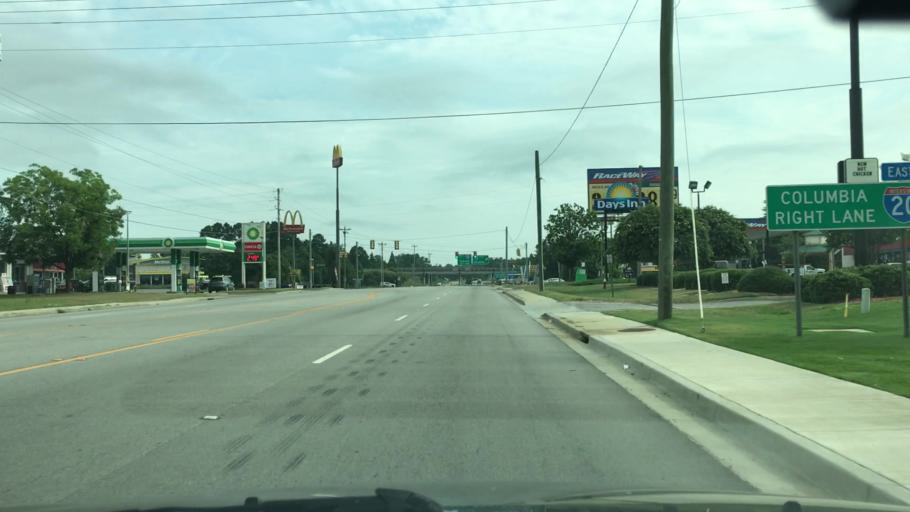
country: US
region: South Carolina
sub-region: Aiken County
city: Aiken
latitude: 33.6628
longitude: -81.6743
